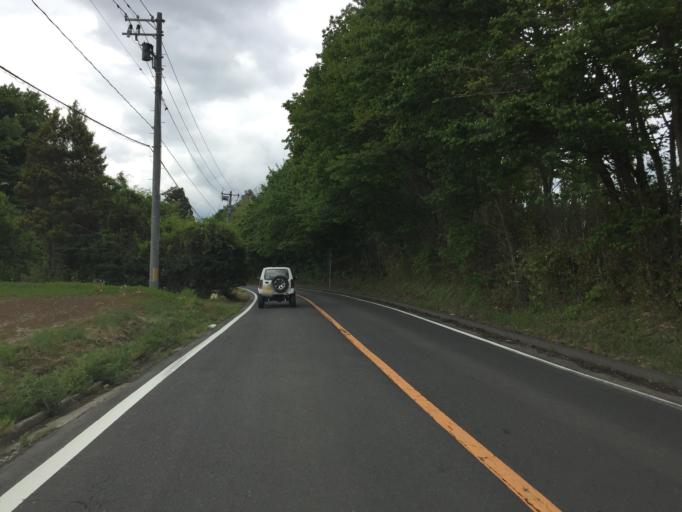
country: JP
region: Fukushima
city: Ishikawa
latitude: 37.1948
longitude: 140.3829
